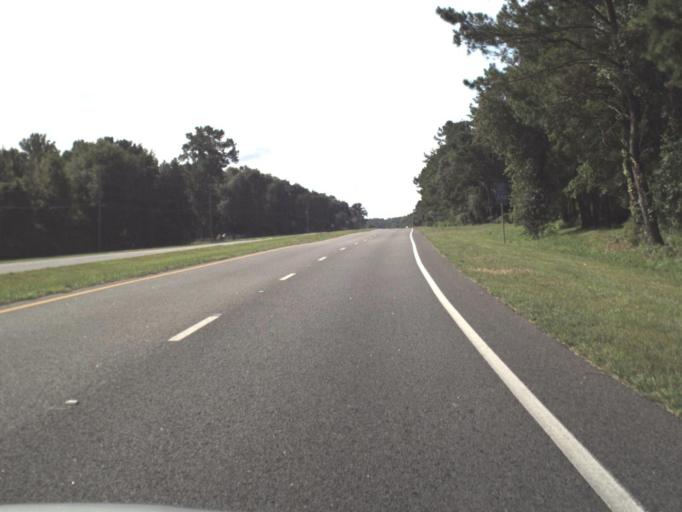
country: US
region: Florida
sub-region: Alachua County
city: Gainesville
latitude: 29.5081
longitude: -82.2705
